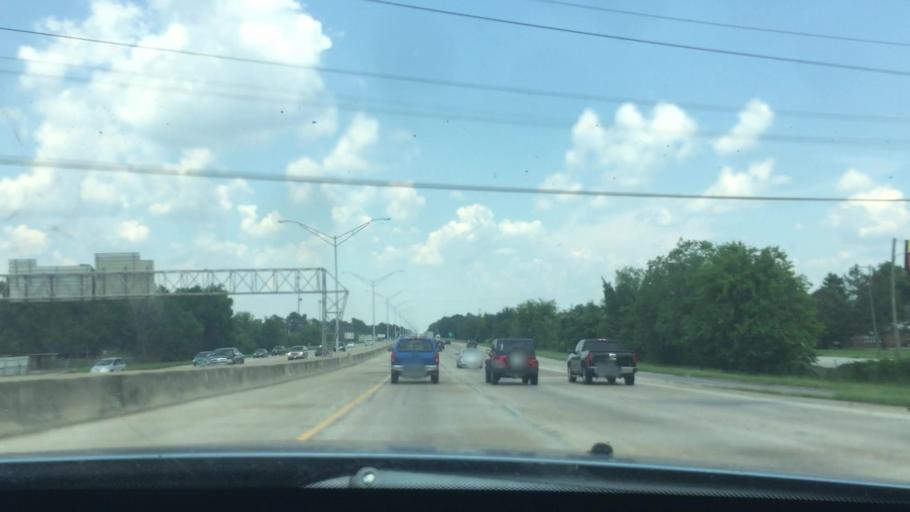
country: US
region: Louisiana
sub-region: East Baton Rouge Parish
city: Westminster
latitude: 30.4309
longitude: -91.0535
